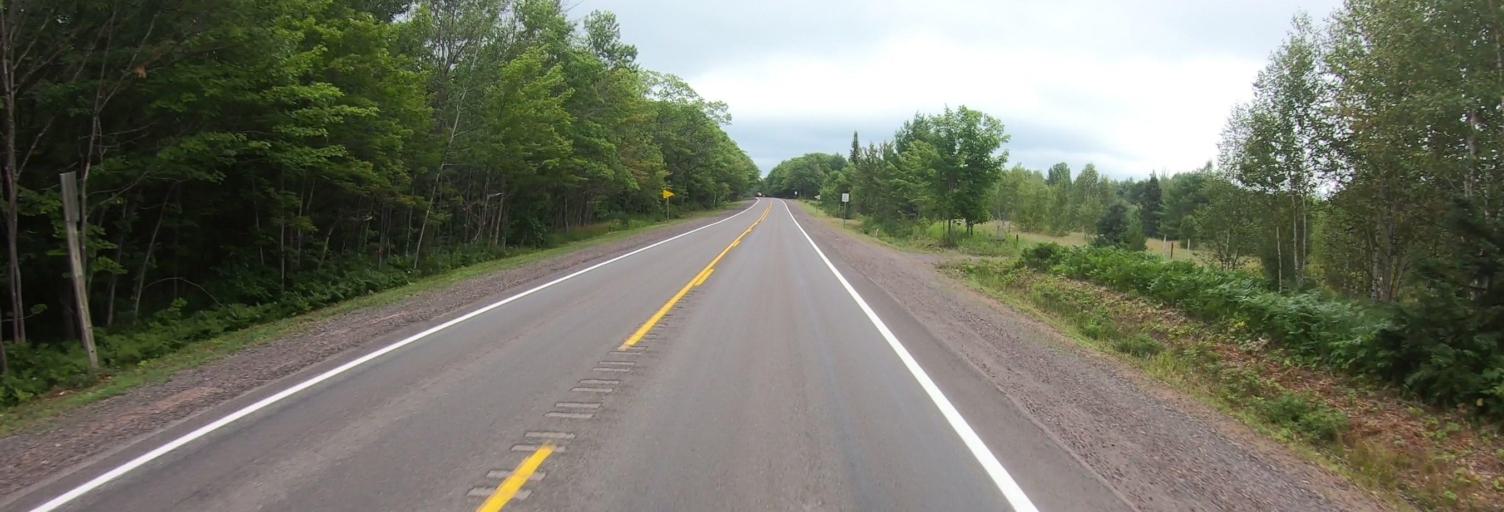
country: US
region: Michigan
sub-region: Keweenaw County
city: Eagle River
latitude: 47.3174
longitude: -88.3446
